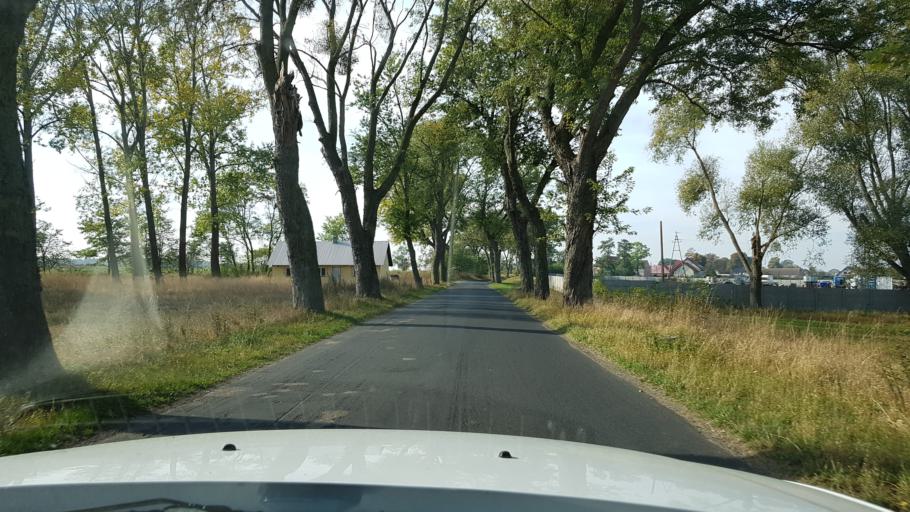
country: PL
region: West Pomeranian Voivodeship
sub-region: Powiat mysliborski
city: Barlinek
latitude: 52.9609
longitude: 15.1343
